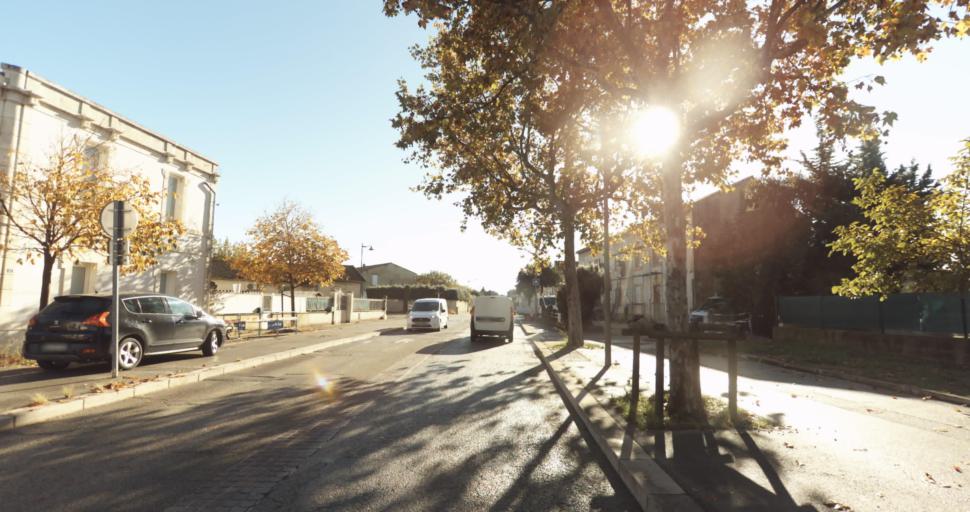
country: FR
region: Provence-Alpes-Cote d'Azur
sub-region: Departement des Bouches-du-Rhone
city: Rognonas
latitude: 43.8975
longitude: 4.8041
